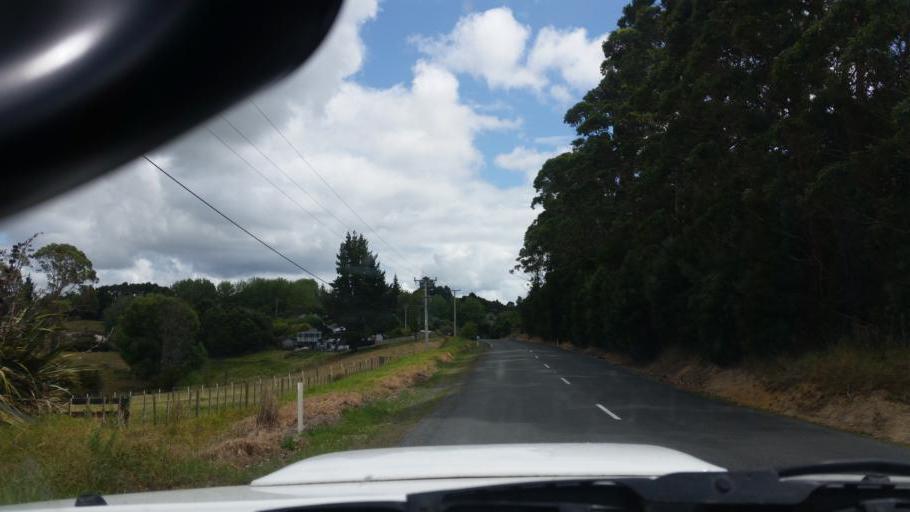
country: NZ
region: Auckland
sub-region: Auckland
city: Wellsford
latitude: -36.1333
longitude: 174.5565
